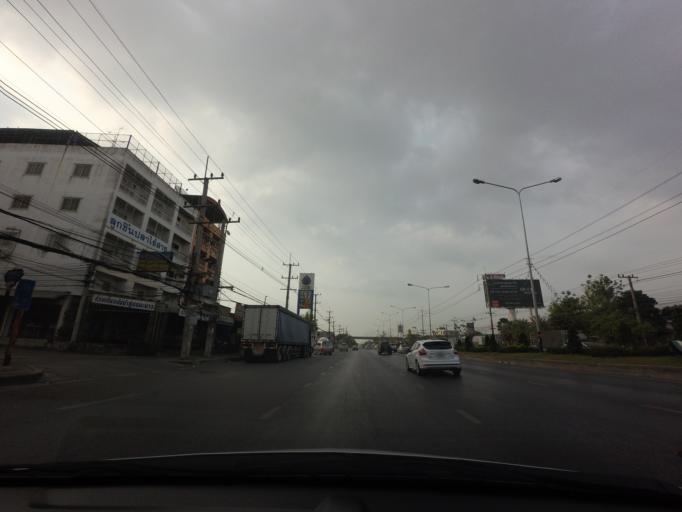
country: TH
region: Bangkok
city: Thawi Watthana
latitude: 13.7483
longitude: 100.3292
